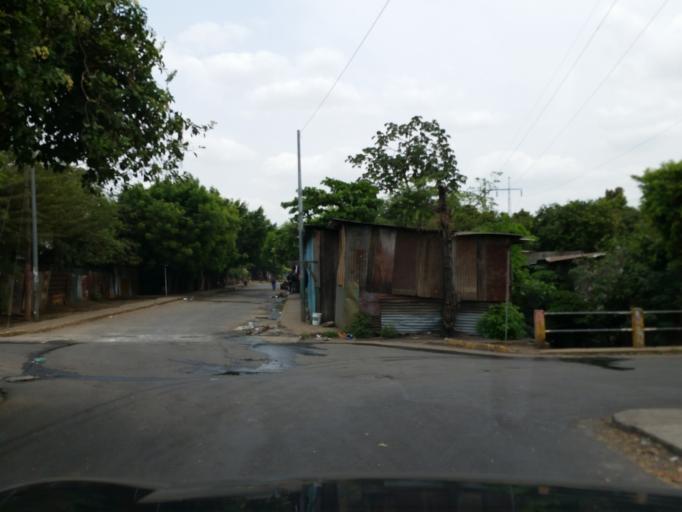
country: NI
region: Managua
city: Managua
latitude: 12.1353
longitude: -86.2329
